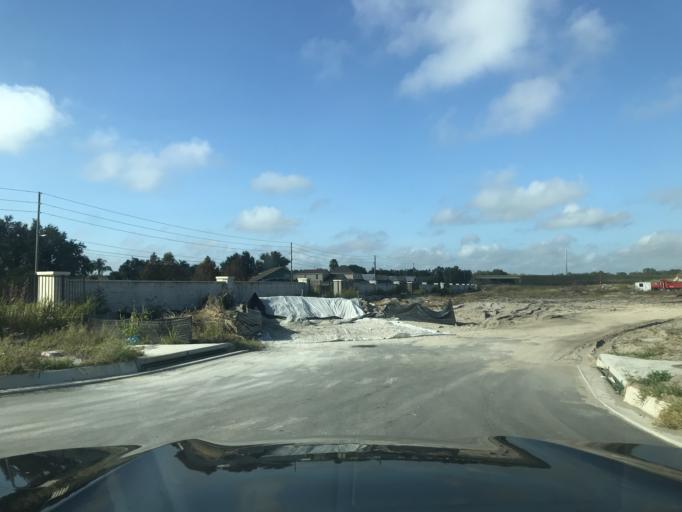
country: US
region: Florida
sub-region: Polk County
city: Citrus Ridge
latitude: 28.3328
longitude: -81.6095
